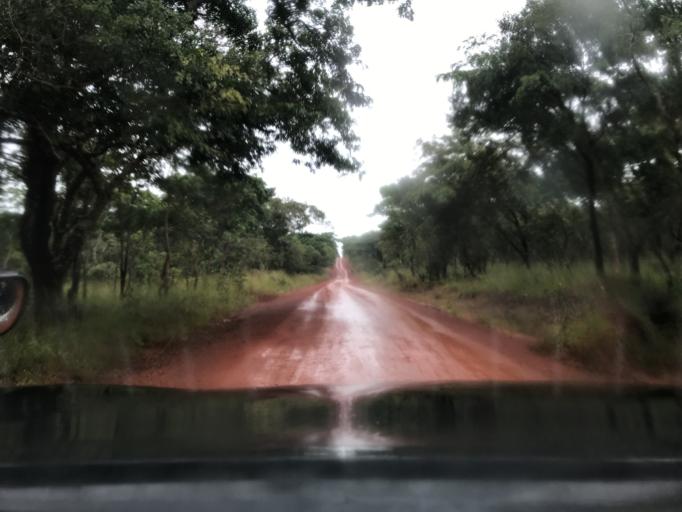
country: TZ
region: Kigoma
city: Uvinza
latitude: -5.2959
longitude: 30.3740
